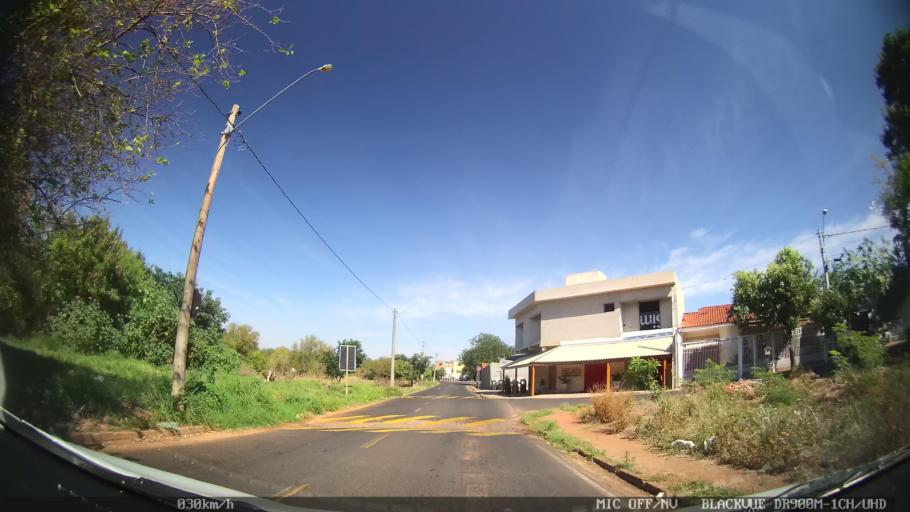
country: BR
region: Sao Paulo
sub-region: Sao Jose Do Rio Preto
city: Sao Jose do Rio Preto
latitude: -20.7701
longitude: -49.3987
